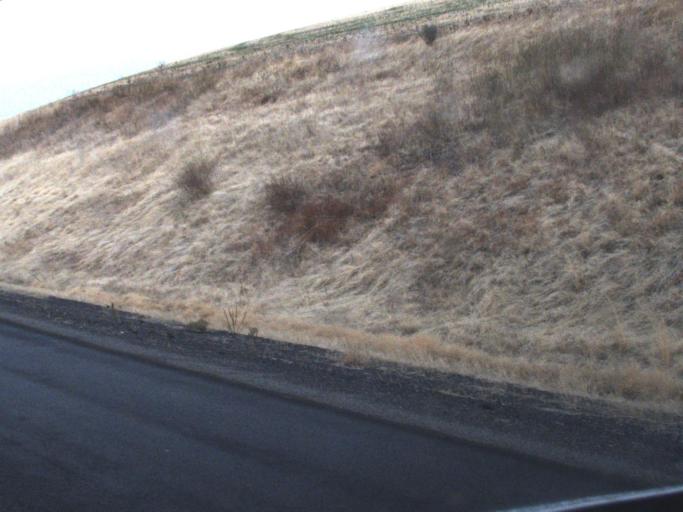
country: US
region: Washington
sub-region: Whitman County
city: Pullman
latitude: 46.7090
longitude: -117.2126
